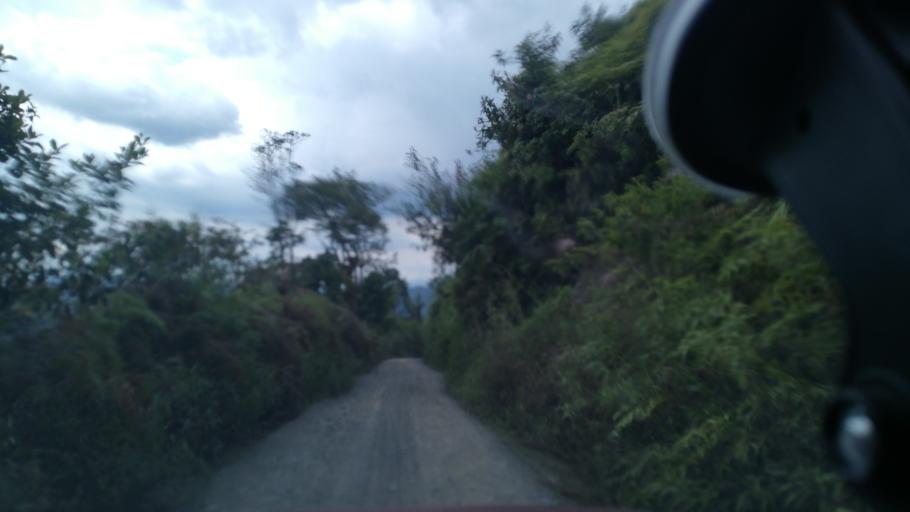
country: CO
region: Cundinamarca
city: Pacho
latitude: 5.1671
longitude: -74.2233
